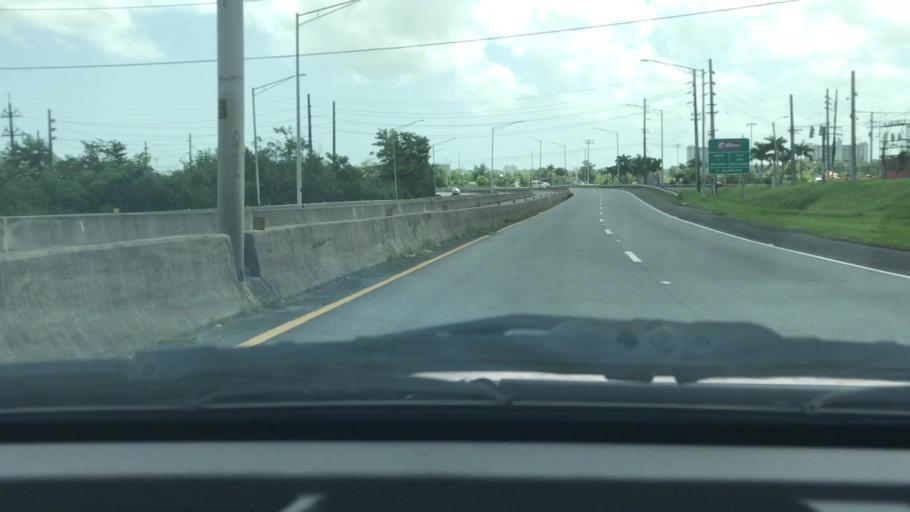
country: PR
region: Bayamon
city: Bayamon
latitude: 18.3825
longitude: -66.1581
